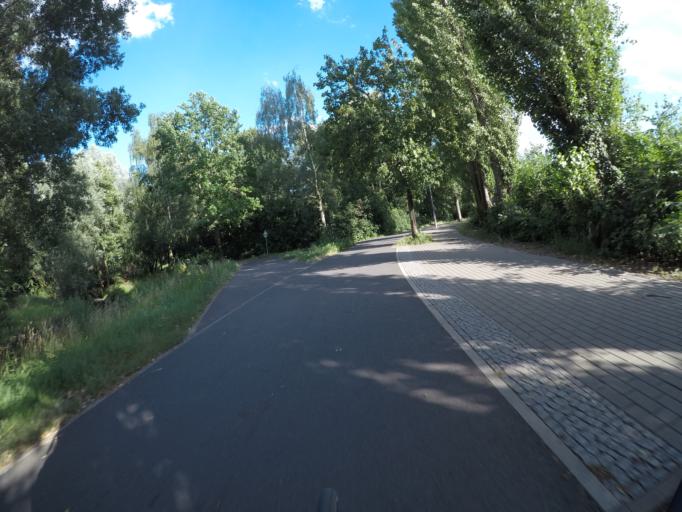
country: DE
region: Berlin
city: Markisches Viertel
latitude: 52.6010
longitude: 13.3499
